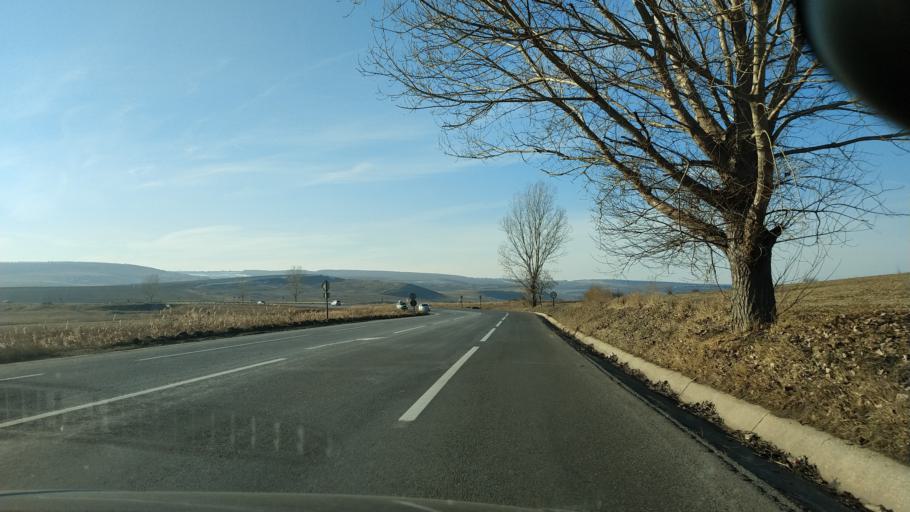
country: RO
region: Iasi
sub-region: Comuna Targu Frumos
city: Targu Frumos
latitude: 47.1981
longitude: 26.9786
